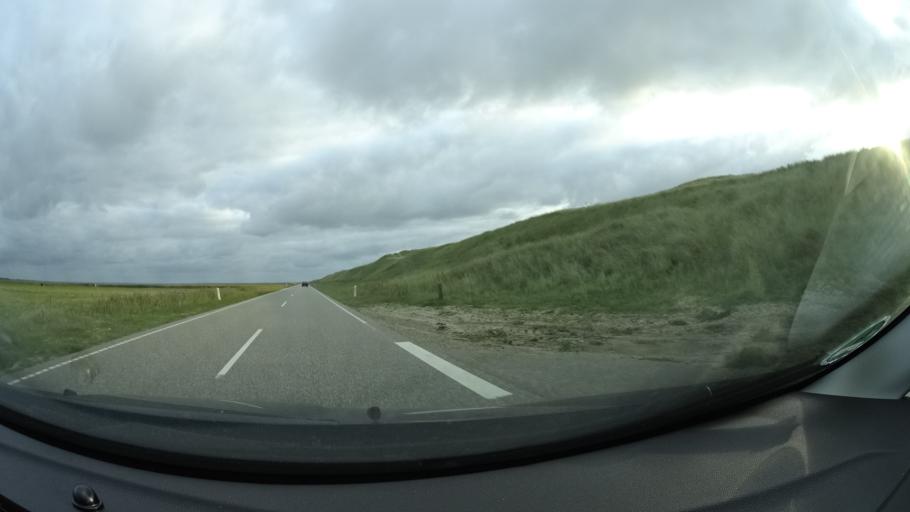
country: DK
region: Central Jutland
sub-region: Lemvig Kommune
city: Harboore
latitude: 56.4248
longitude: 8.1236
